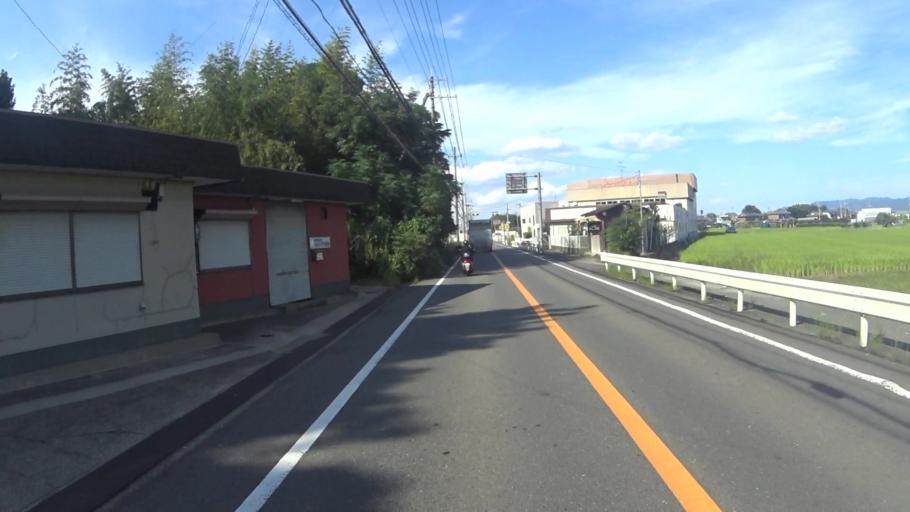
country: JP
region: Kyoto
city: Yawata
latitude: 34.8609
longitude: 135.7453
